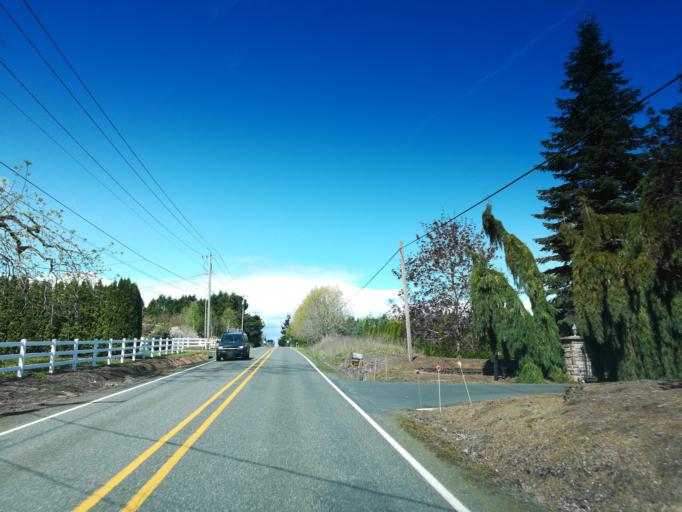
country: US
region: Oregon
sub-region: Clackamas County
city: Damascus
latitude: 45.4261
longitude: -122.4342
